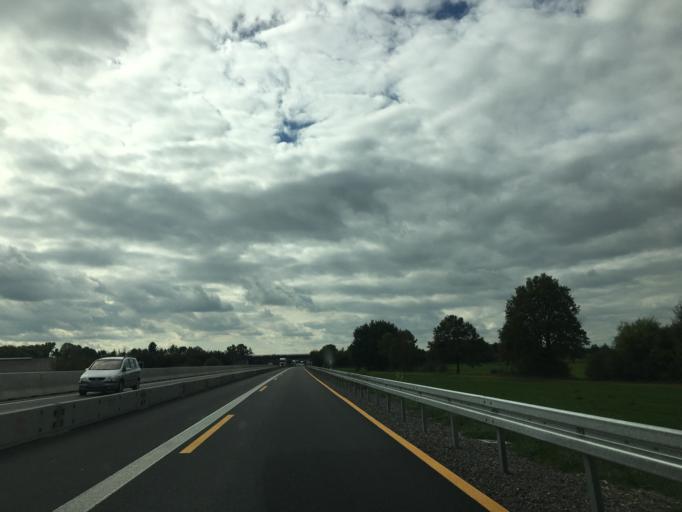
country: DE
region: Baden-Wuerttemberg
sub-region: Freiburg Region
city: Schutterwald
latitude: 48.4181
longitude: 7.8785
